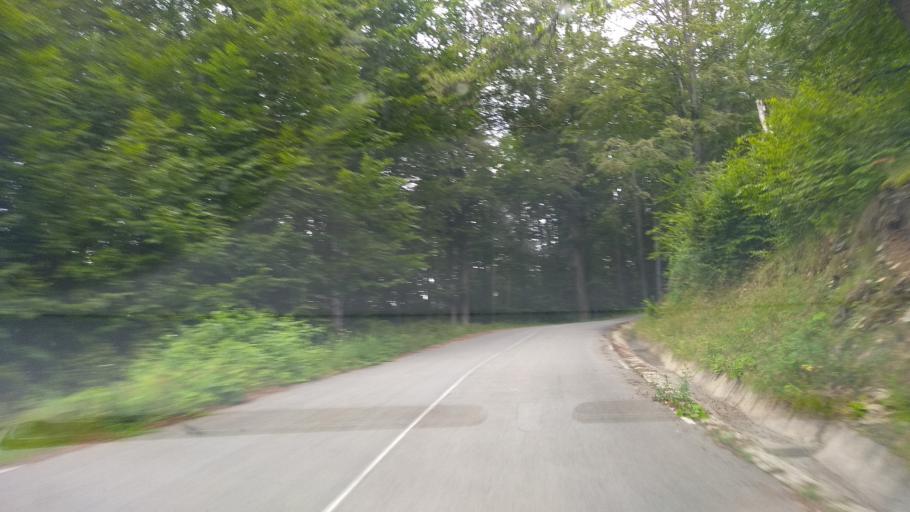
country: RO
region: Hunedoara
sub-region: Municipiul  Vulcan
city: Jiu-Paroseni
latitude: 45.3375
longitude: 23.2913
